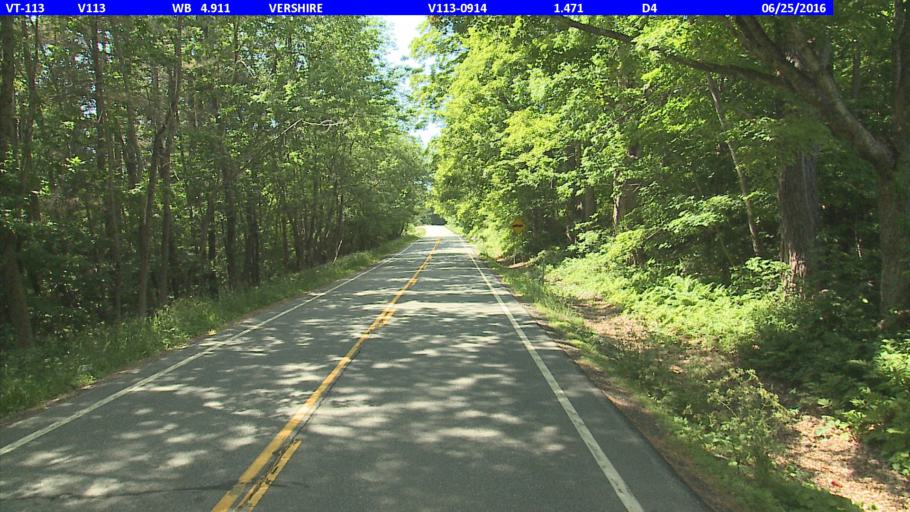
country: US
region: Vermont
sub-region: Orange County
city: Chelsea
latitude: 43.9813
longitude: -72.3598
